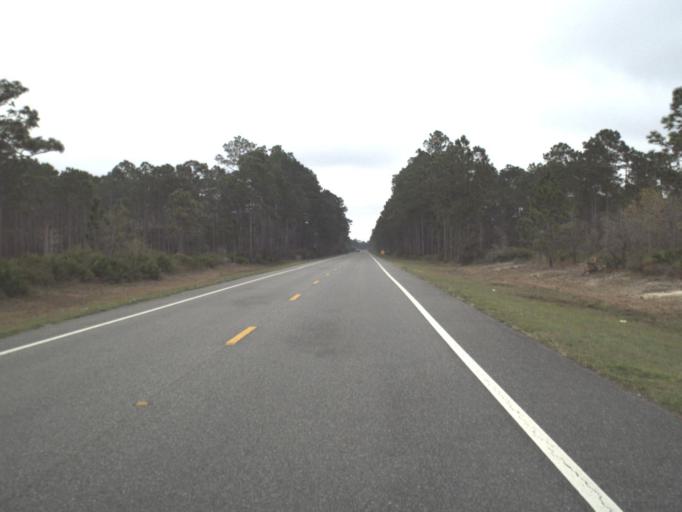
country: US
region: Florida
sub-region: Franklin County
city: Eastpoint
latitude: 29.8117
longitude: -84.8425
